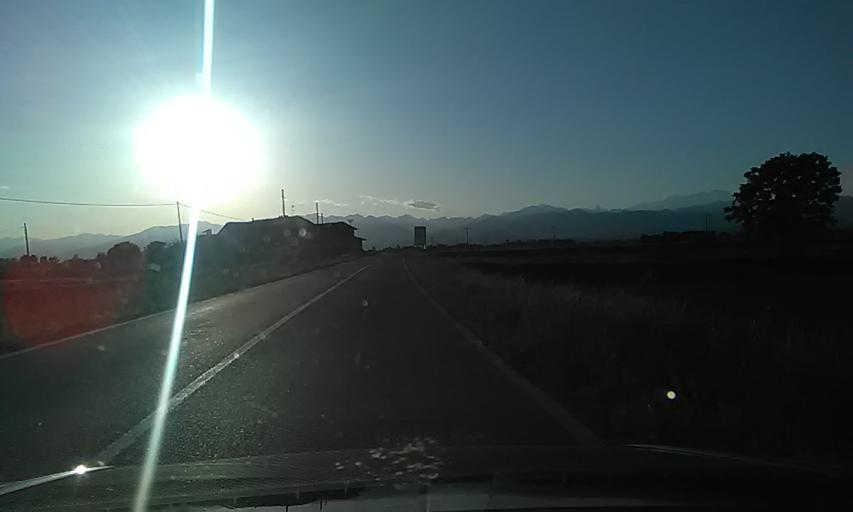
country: IT
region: Piedmont
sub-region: Provincia di Vercelli
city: San Giacomo Vercellese
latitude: 45.5213
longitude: 8.3407
